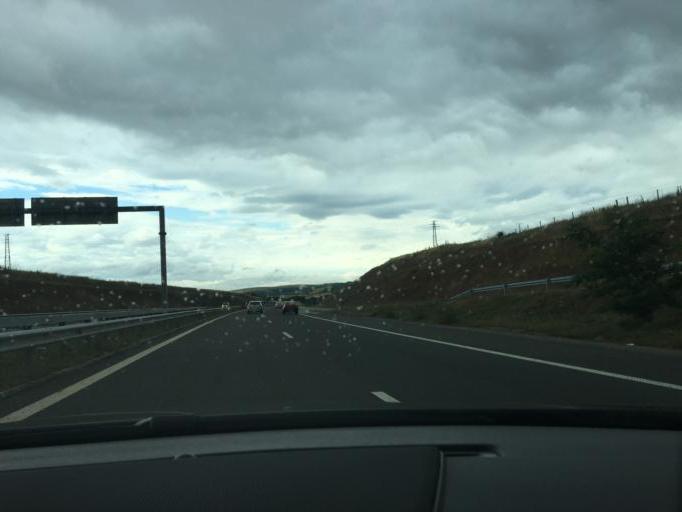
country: BG
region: Kyustendil
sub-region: Obshtina Dupnitsa
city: Dupnitsa
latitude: 42.3303
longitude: 23.0991
